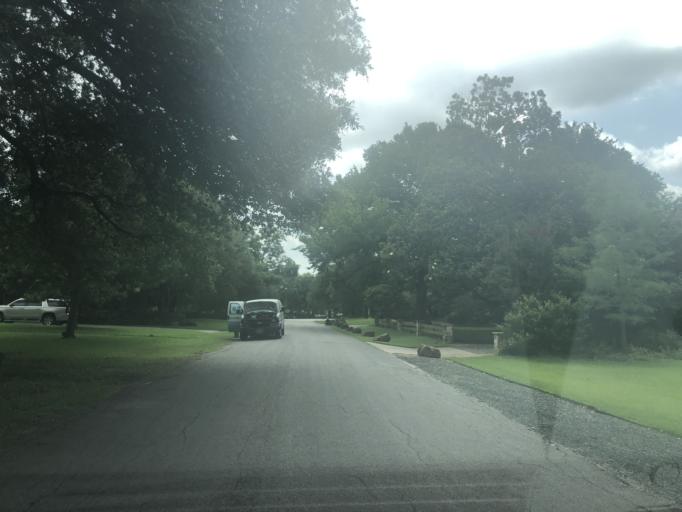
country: US
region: Texas
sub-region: Dallas County
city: University Park
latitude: 32.8676
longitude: -96.8321
